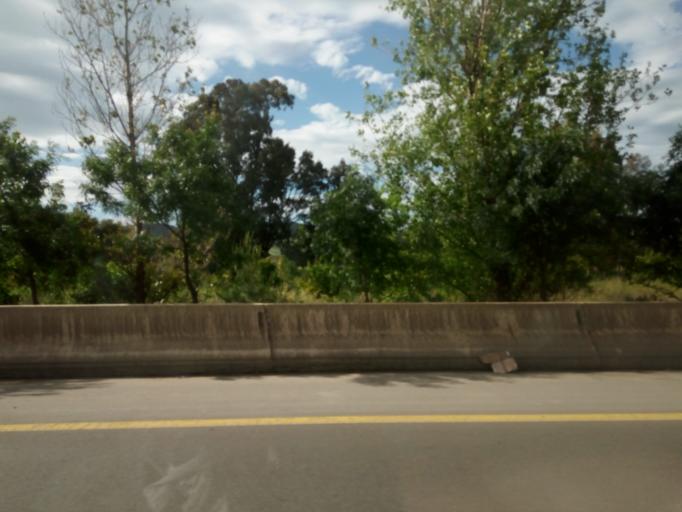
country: DZ
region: Tipaza
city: El Affroun
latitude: 36.4449
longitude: 2.5857
